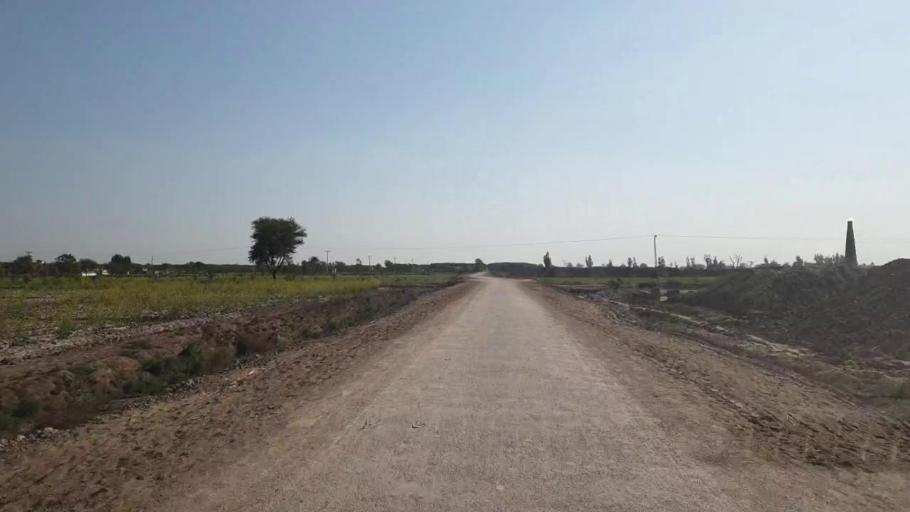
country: PK
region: Sindh
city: Tando Allahyar
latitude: 25.4092
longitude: 68.7053
